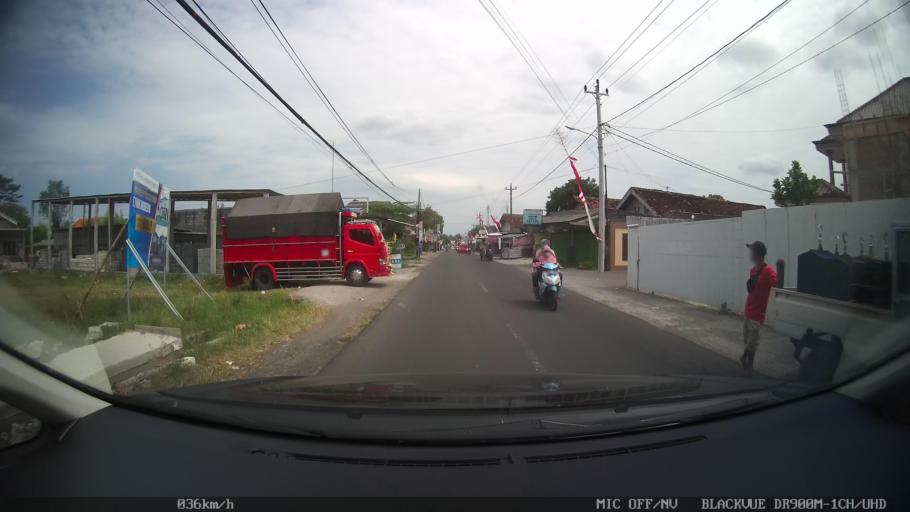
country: ID
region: Daerah Istimewa Yogyakarta
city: Depok
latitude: -7.7419
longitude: 110.4514
